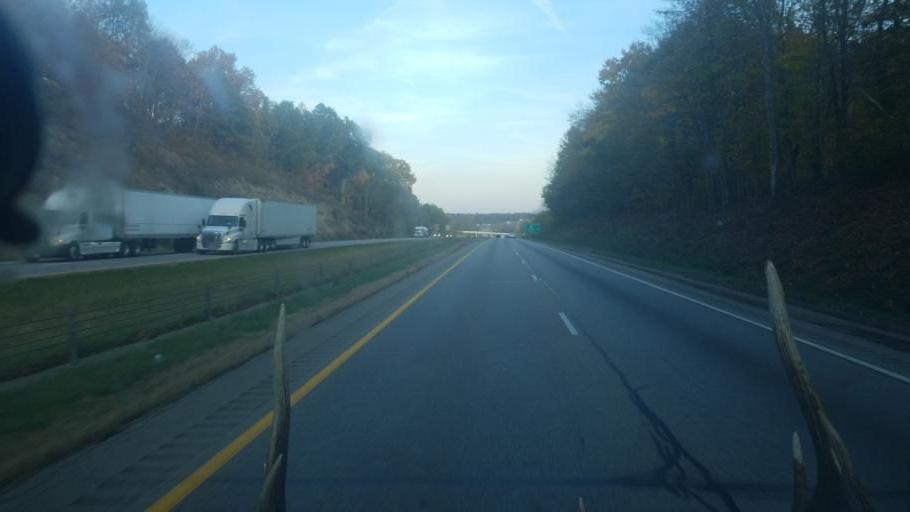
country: US
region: Ohio
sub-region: Perry County
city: Somerset
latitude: 39.9364
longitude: -82.2669
